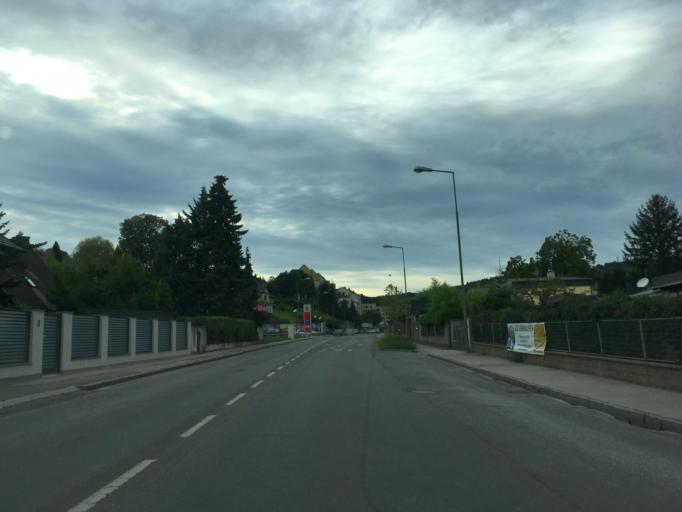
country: AT
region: Lower Austria
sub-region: Politischer Bezirk Wien-Umgebung
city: Klosterneuburg
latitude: 48.3061
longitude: 16.2897
